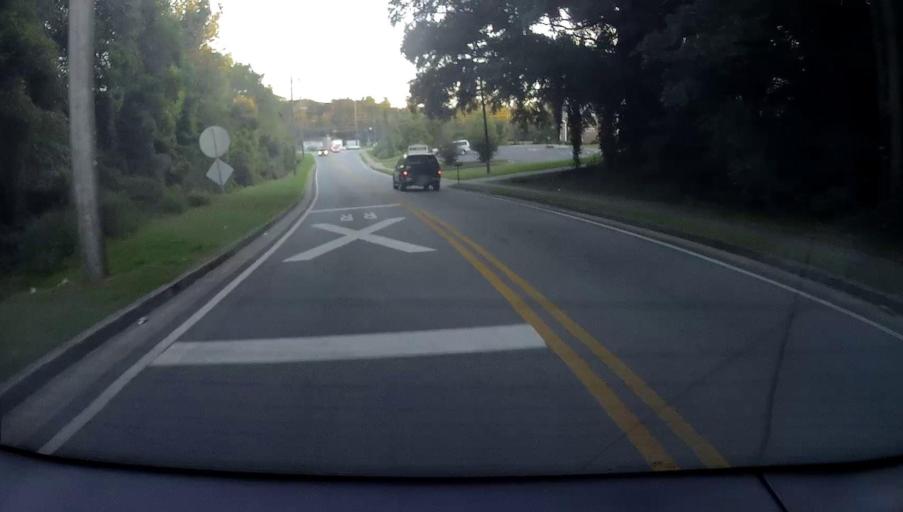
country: US
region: Georgia
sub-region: Houston County
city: Perry
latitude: 32.4583
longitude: -83.7385
